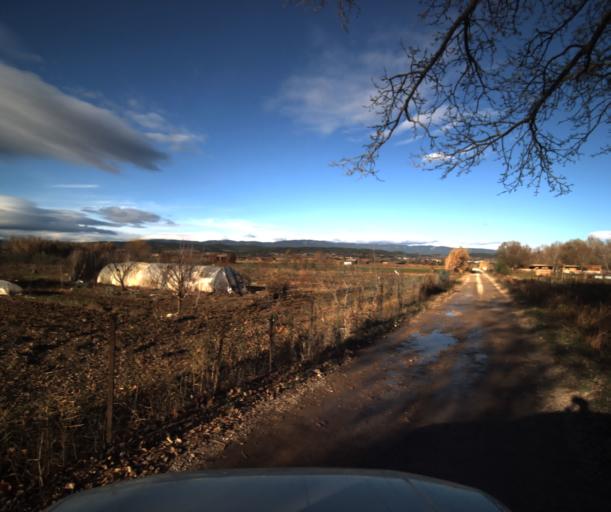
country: FR
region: Provence-Alpes-Cote d'Azur
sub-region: Departement du Vaucluse
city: Pertuis
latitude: 43.6769
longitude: 5.4784
